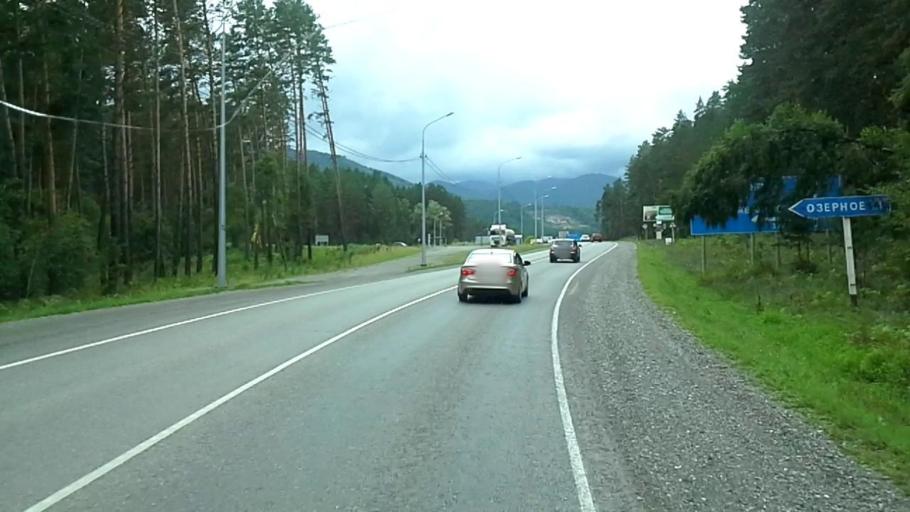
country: RU
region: Altay
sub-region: Mayminskiy Rayon
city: Manzherok
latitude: 51.8229
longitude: 85.7886
